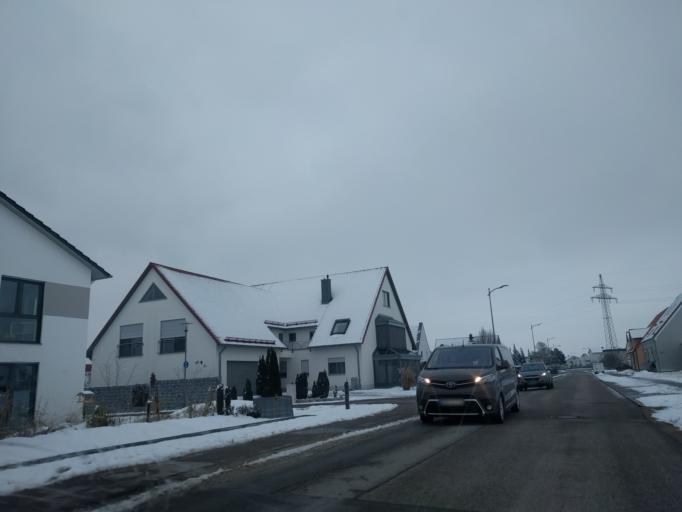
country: DE
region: Bavaria
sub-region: Swabia
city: Donauwoerth
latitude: 48.7172
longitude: 10.7464
